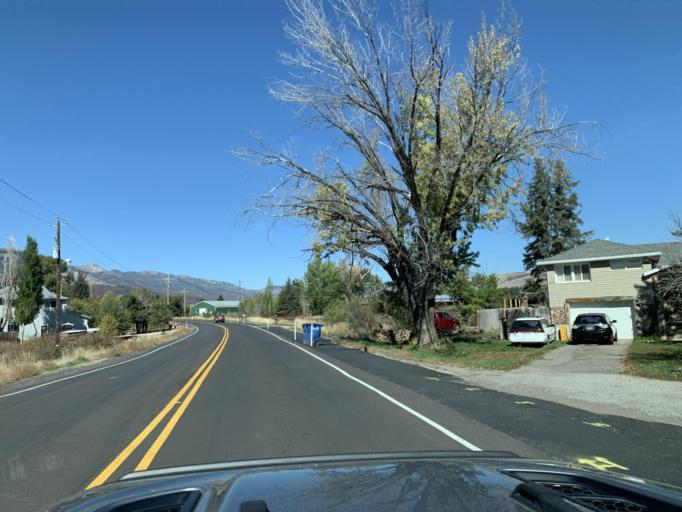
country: US
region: Utah
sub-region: Weber County
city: Wolf Creek
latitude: 41.3116
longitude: -111.8352
